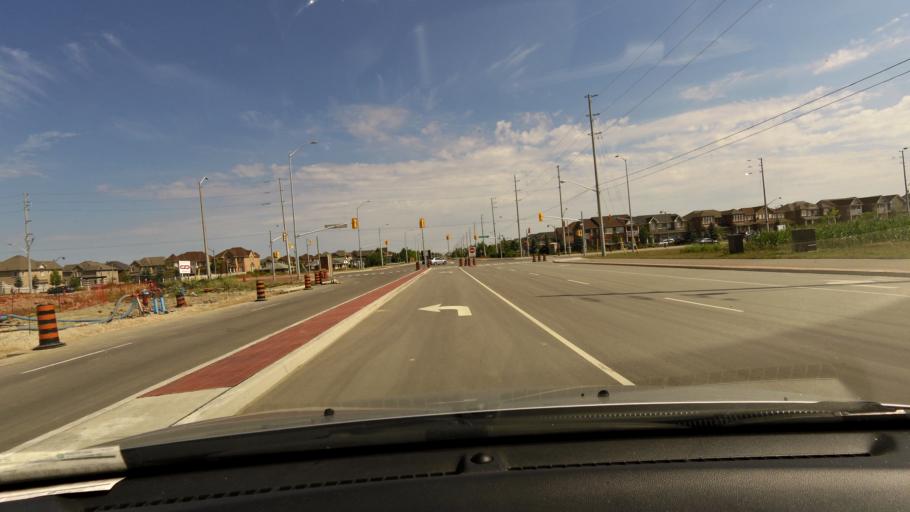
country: CA
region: Ontario
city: Brampton
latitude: 43.7748
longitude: -79.7617
